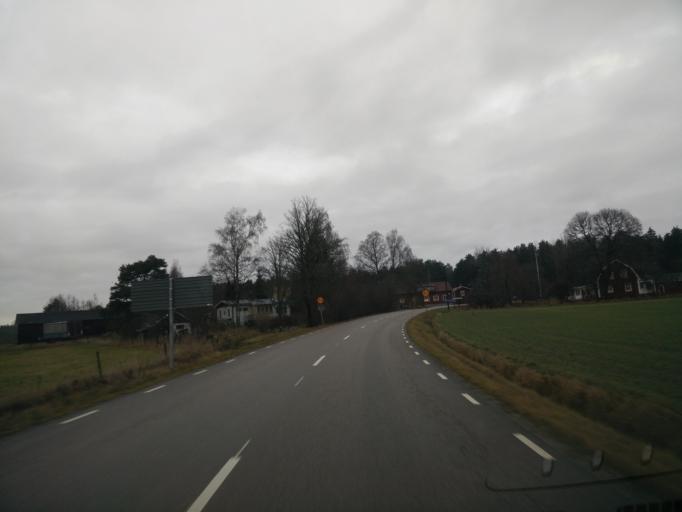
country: SE
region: Uppsala
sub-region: Enkopings Kommun
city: Enkoping
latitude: 59.8117
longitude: 17.0998
